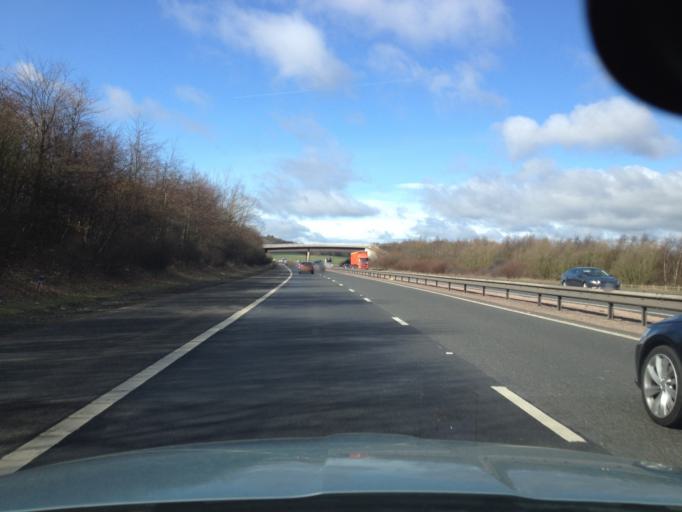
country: GB
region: Scotland
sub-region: Edinburgh
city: Ratho
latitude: 55.9300
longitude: -3.3602
